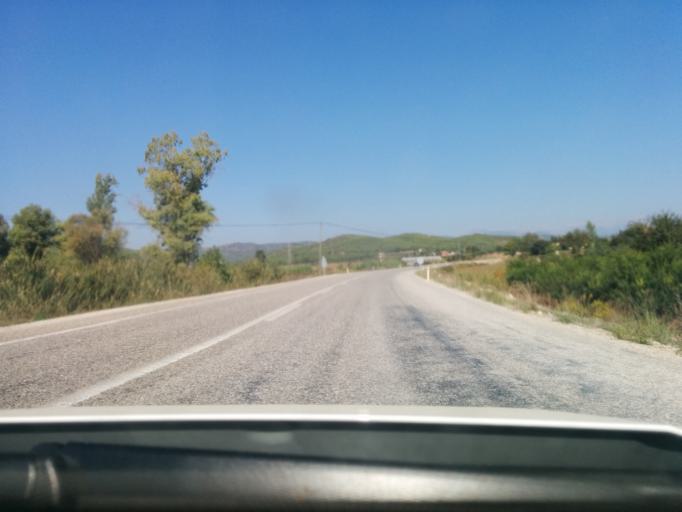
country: TR
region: Mugla
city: Kemer
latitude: 36.5637
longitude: 29.3465
